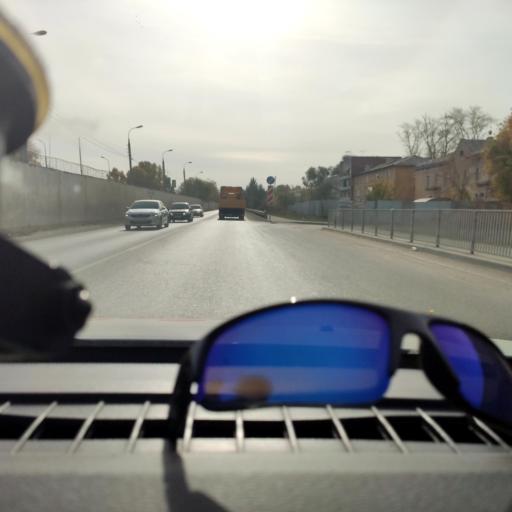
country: RU
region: Samara
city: Samara
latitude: 53.1349
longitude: 50.1050
